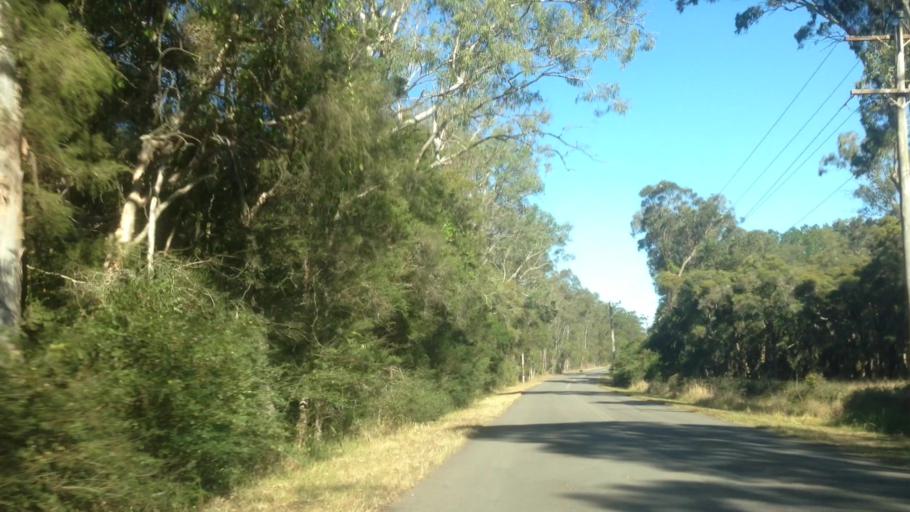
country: AU
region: New South Wales
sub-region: Lake Macquarie Shire
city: Cooranbong
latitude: -33.0966
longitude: 151.4529
